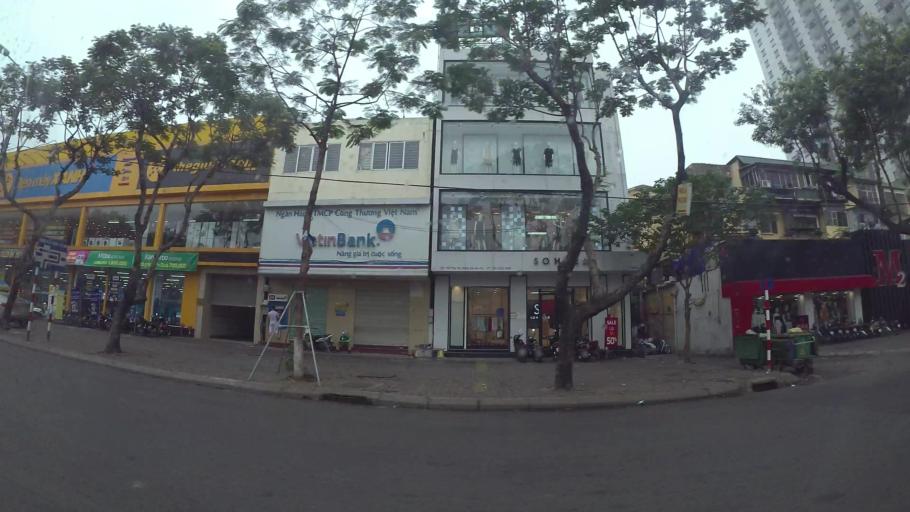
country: VN
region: Ha Noi
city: Dong Da
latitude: 21.0141
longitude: 105.8183
